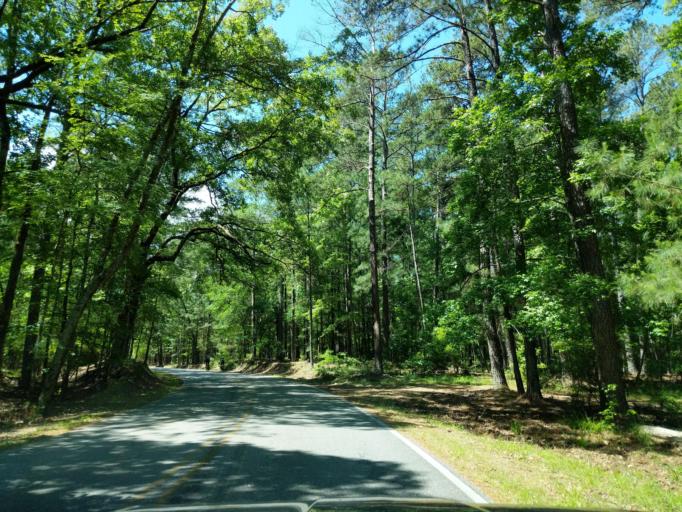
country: US
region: Georgia
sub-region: Columbia County
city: Appling
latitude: 33.6570
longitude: -82.3873
